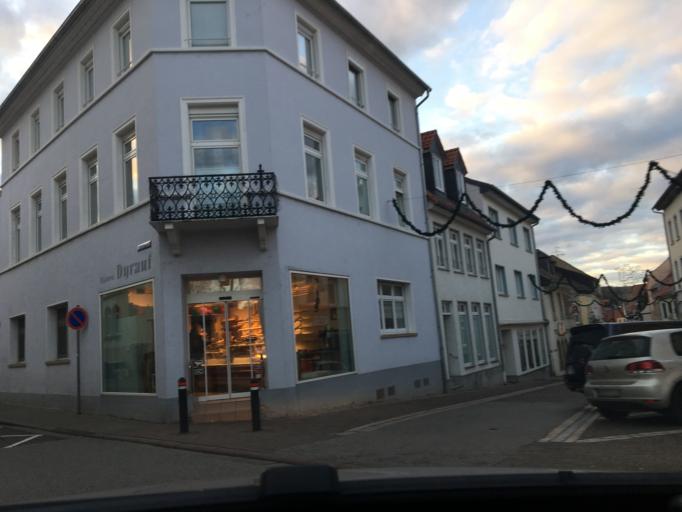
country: DE
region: Rheinland-Pfalz
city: Alzey
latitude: 49.7439
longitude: 8.1151
